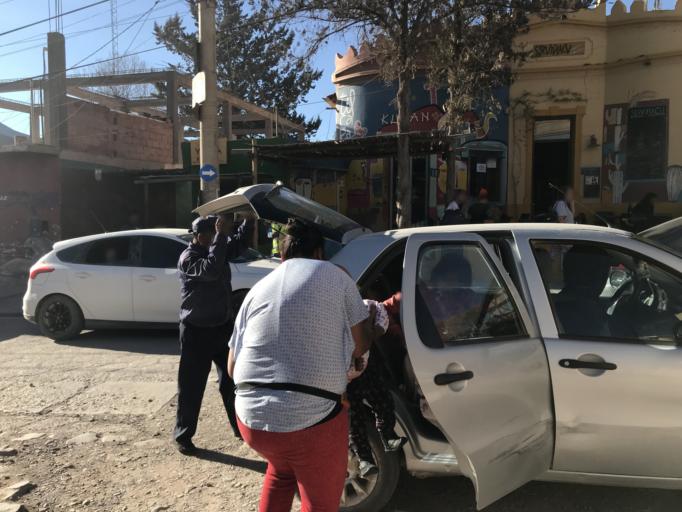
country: AR
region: Jujuy
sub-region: Departamento de Tilcara
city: Tilcara
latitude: -23.5768
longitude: -65.3958
